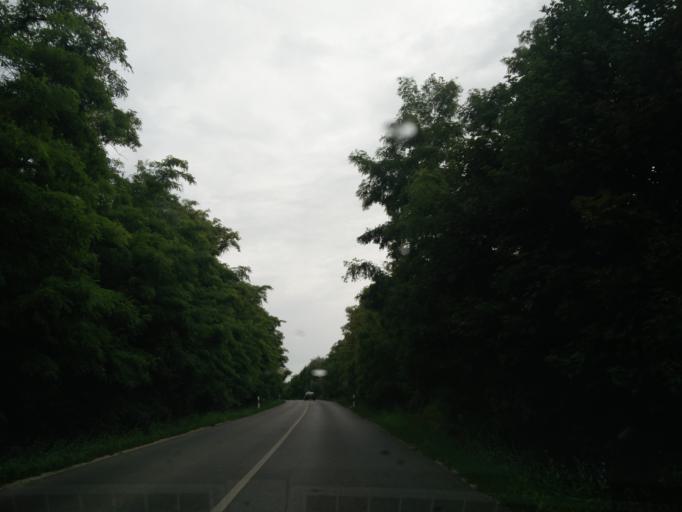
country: HU
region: Pest
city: Biatorbagy
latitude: 47.4569
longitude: 18.8027
